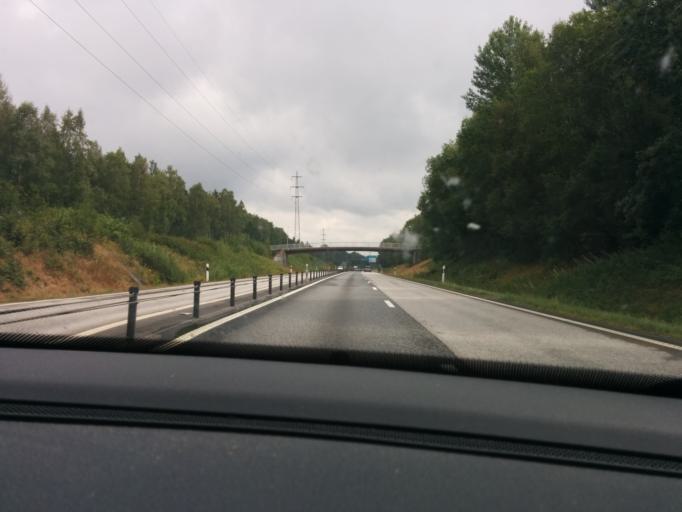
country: SE
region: Kronoberg
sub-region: Vaxjo Kommun
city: Vaexjoe
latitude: 56.9016
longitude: 14.8013
